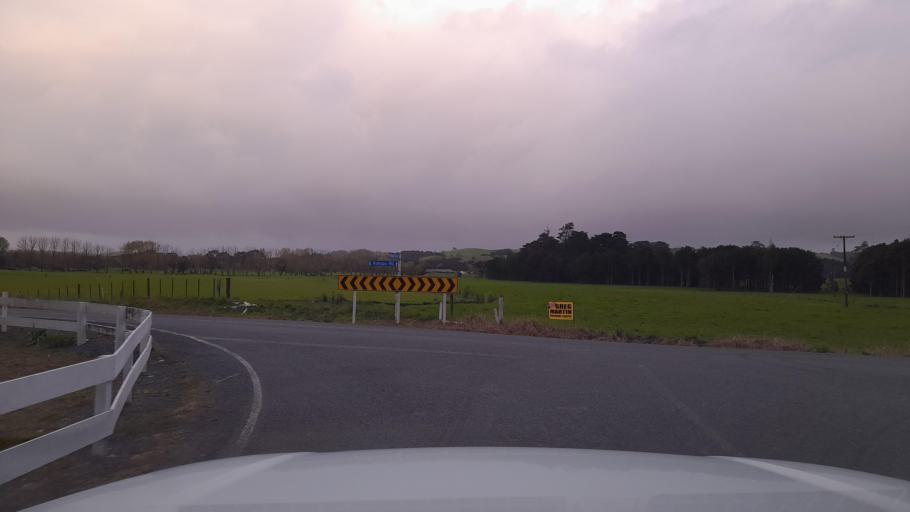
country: NZ
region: Northland
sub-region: Whangarei
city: Maungatapere
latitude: -35.7109
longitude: 174.1750
